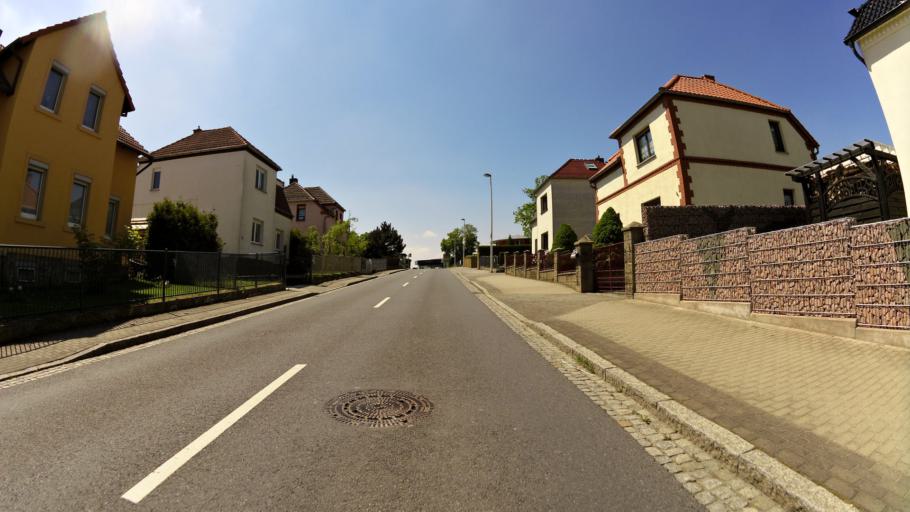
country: DE
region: Saxony
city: Riesa
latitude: 51.2964
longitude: 13.2497
